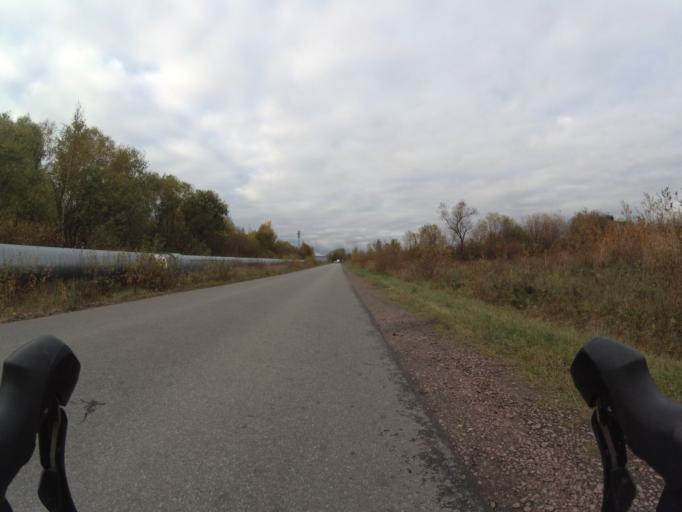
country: RU
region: St.-Petersburg
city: Lakhtinskiy
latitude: 59.9995
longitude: 30.1574
